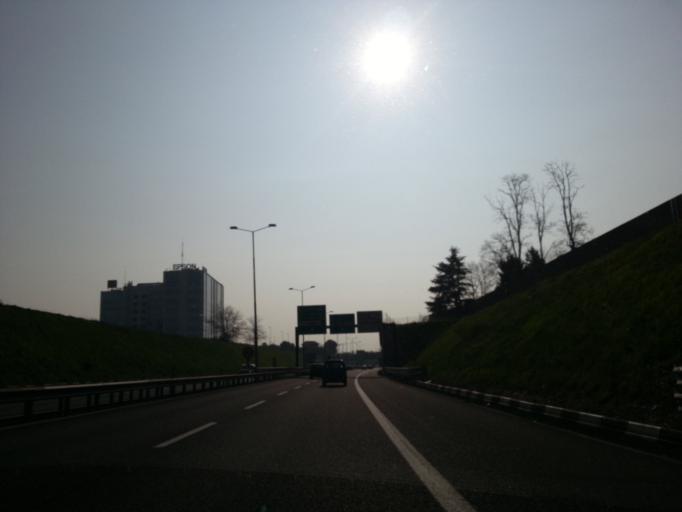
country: IT
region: Lombardy
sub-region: Citta metropolitana di Milano
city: Cinisello Balsamo
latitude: 45.5635
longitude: 9.2355
